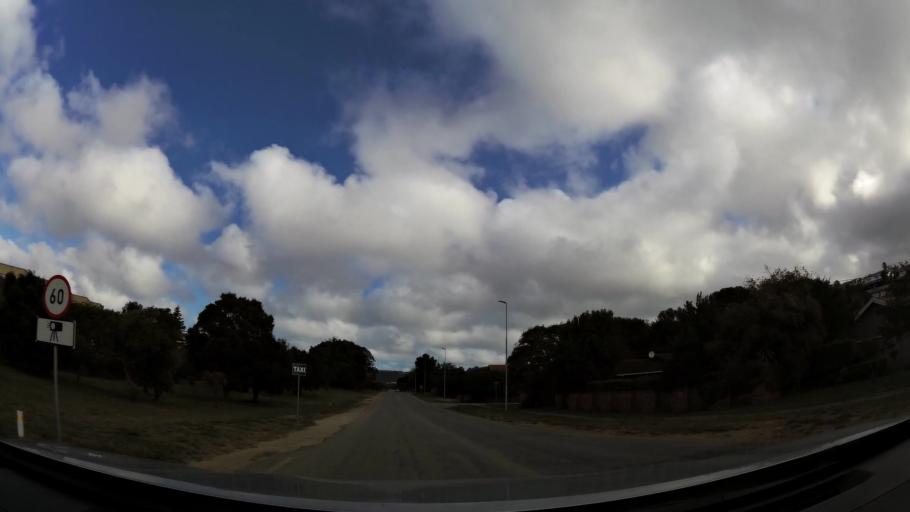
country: ZA
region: Western Cape
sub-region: Eden District Municipality
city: Plettenberg Bay
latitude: -34.0695
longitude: 23.3691
